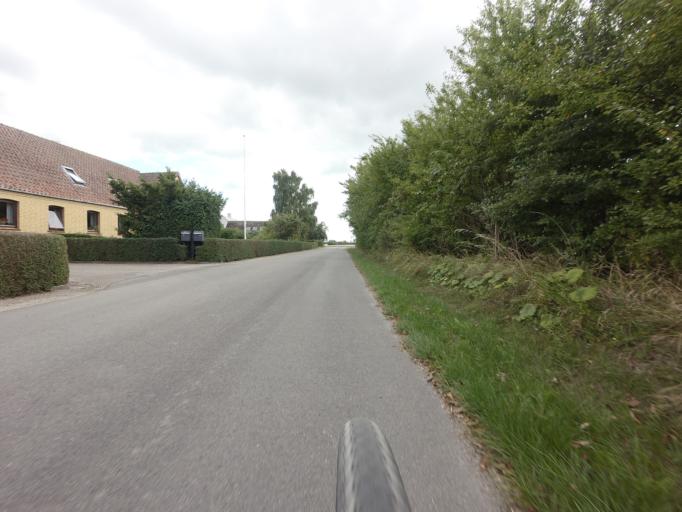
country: DK
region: Zealand
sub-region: Vordingborg Kommune
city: Stege
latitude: 55.0115
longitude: 12.3263
